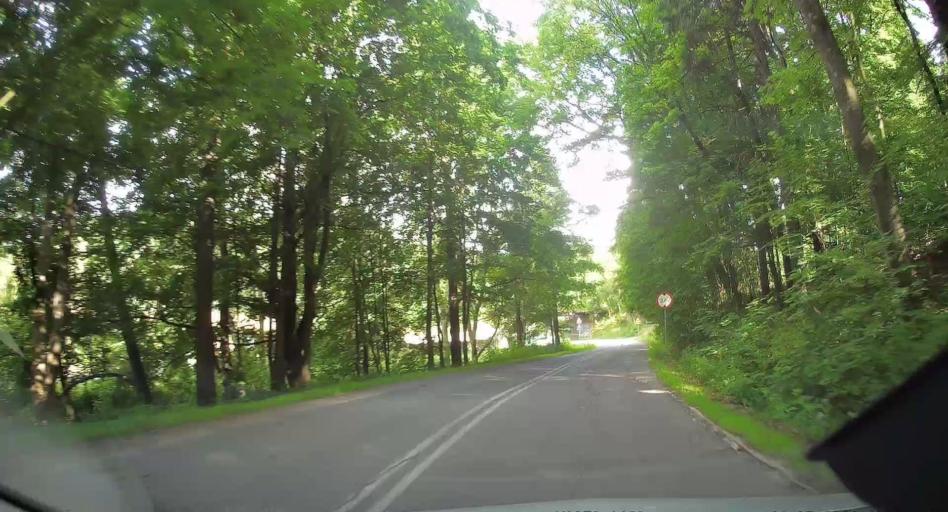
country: PL
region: Lower Silesian Voivodeship
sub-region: Powiat walbrzyski
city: Walim
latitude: 50.7295
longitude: 16.4057
